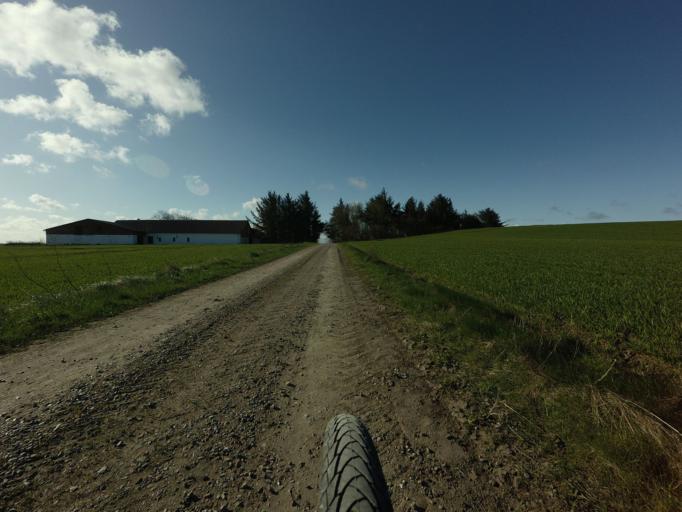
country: DK
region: North Denmark
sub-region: Hjorring Kommune
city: Vra
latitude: 57.3650
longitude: 9.8167
